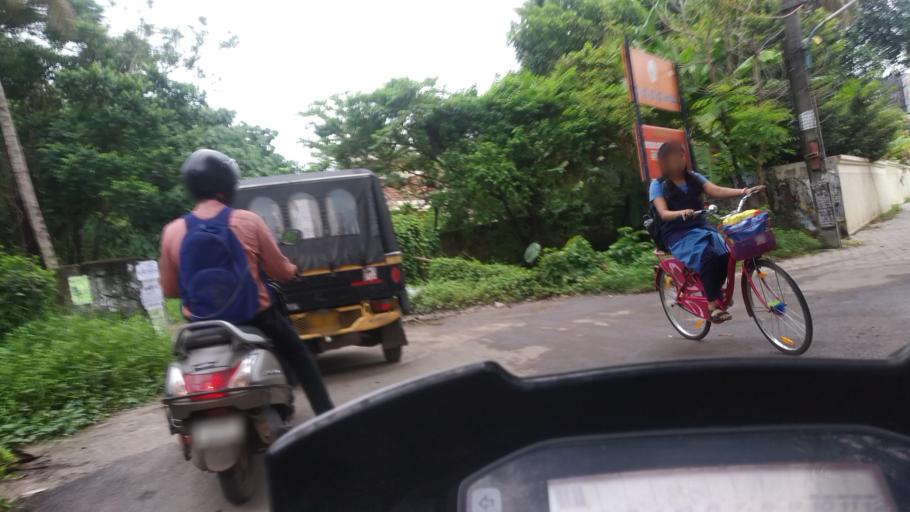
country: IN
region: Kerala
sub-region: Ernakulam
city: Cochin
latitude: 9.9956
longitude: 76.3000
